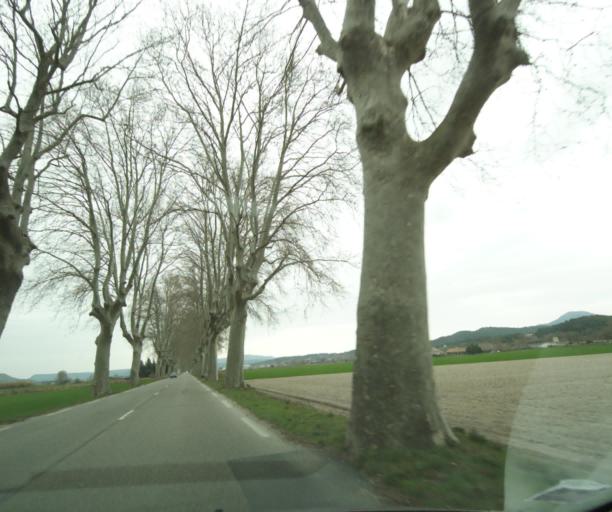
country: FR
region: Provence-Alpes-Cote d'Azur
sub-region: Departement des Bouches-du-Rhone
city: Meyrargues
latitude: 43.6437
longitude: 5.5495
